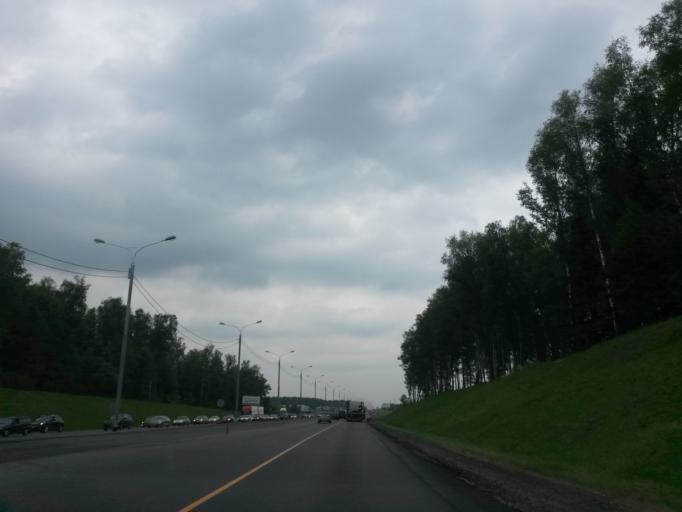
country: RU
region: Moskovskaya
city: Lyubuchany
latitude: 55.2462
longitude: 37.5284
